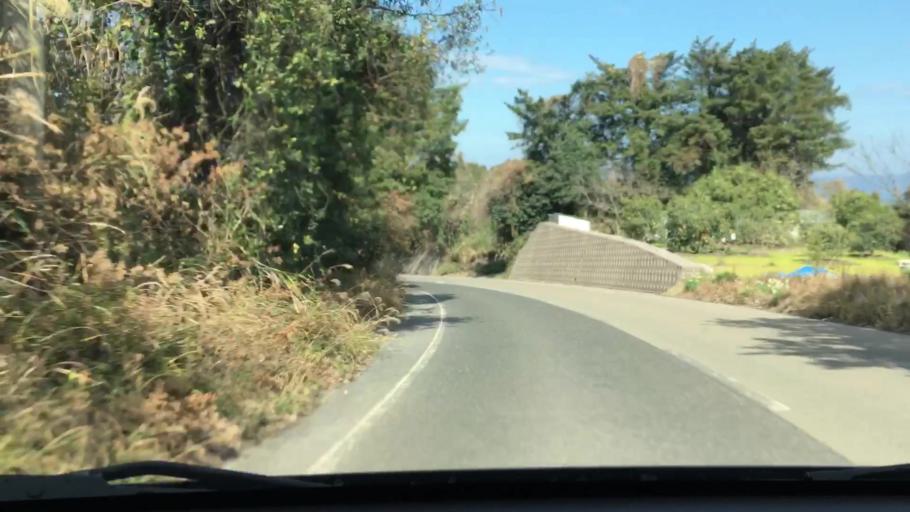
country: JP
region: Kagoshima
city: Kajiki
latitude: 31.6215
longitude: 130.6733
